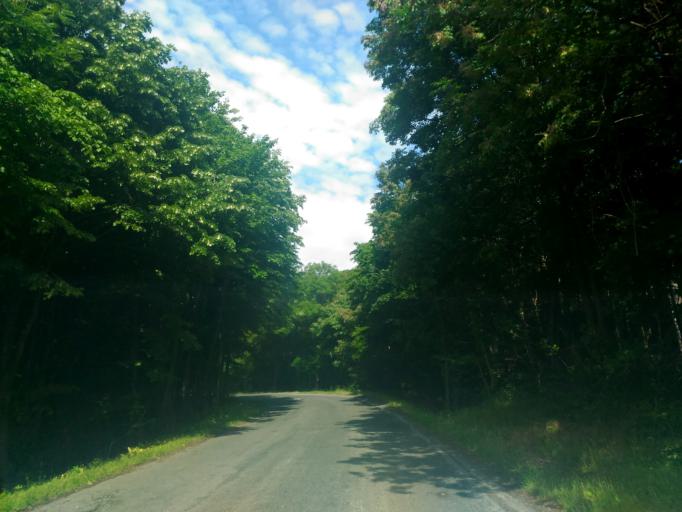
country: HU
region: Baranya
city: Pecs
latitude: 46.1185
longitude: 18.2029
